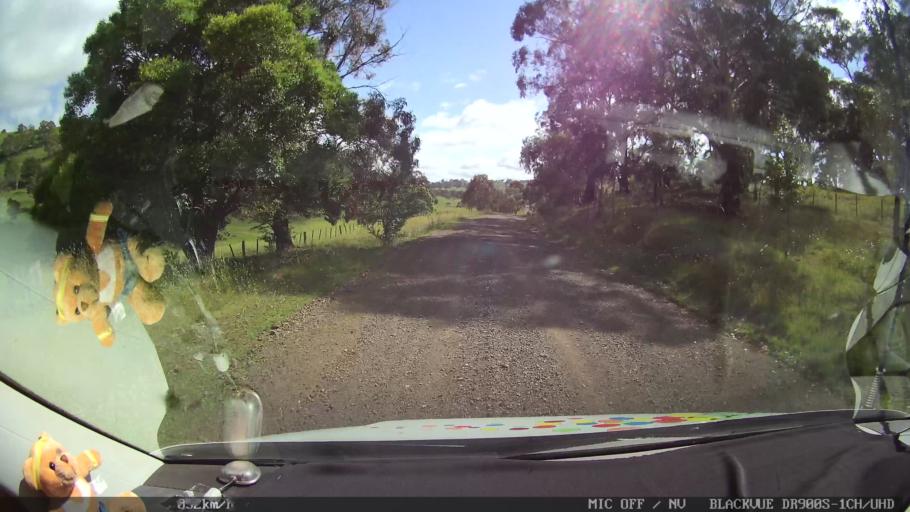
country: AU
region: New South Wales
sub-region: Guyra
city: Guyra
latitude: -29.9884
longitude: 151.6897
